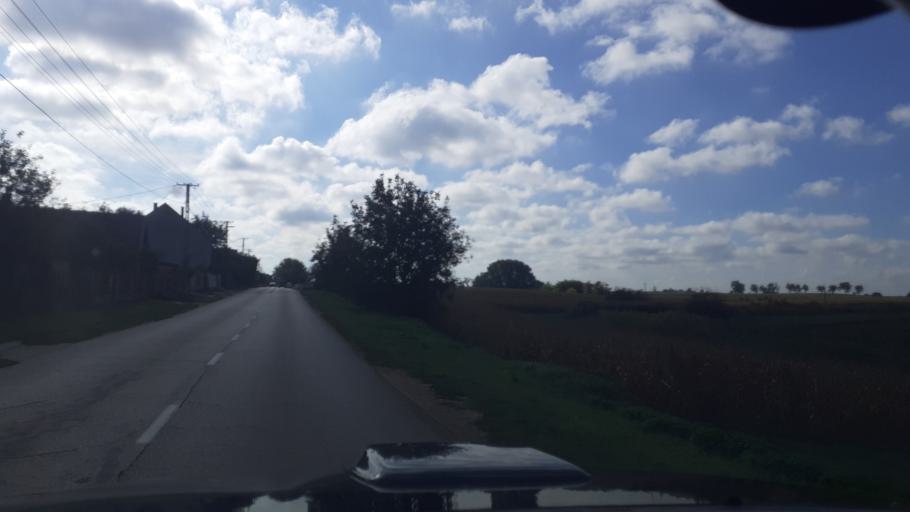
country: HU
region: Fejer
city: Baracs
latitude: 46.9165
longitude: 18.8822
